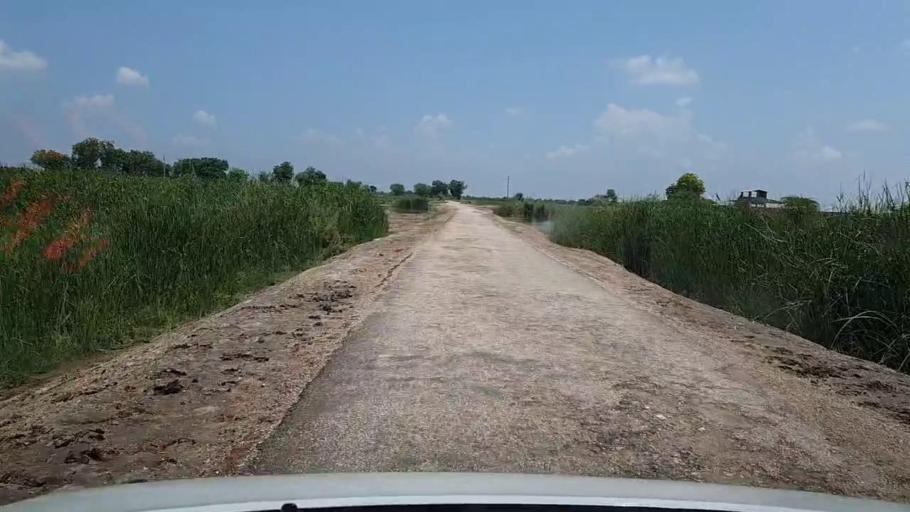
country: PK
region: Sindh
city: Bhiria
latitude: 26.9761
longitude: 68.2083
